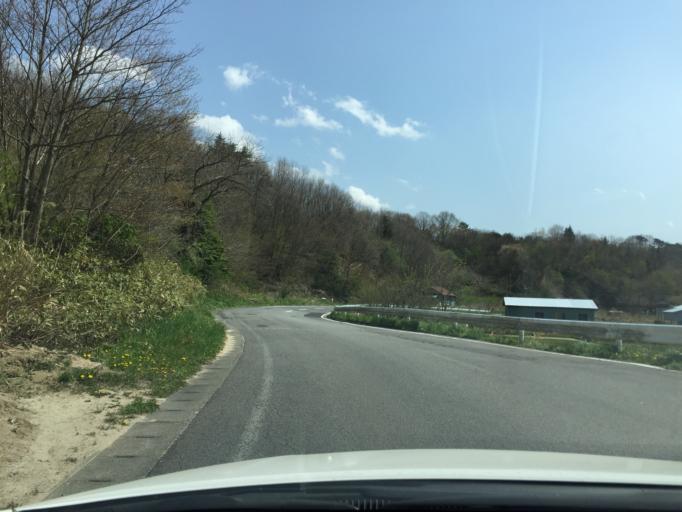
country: JP
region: Fukushima
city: Namie
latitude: 37.3976
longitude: 140.8015
